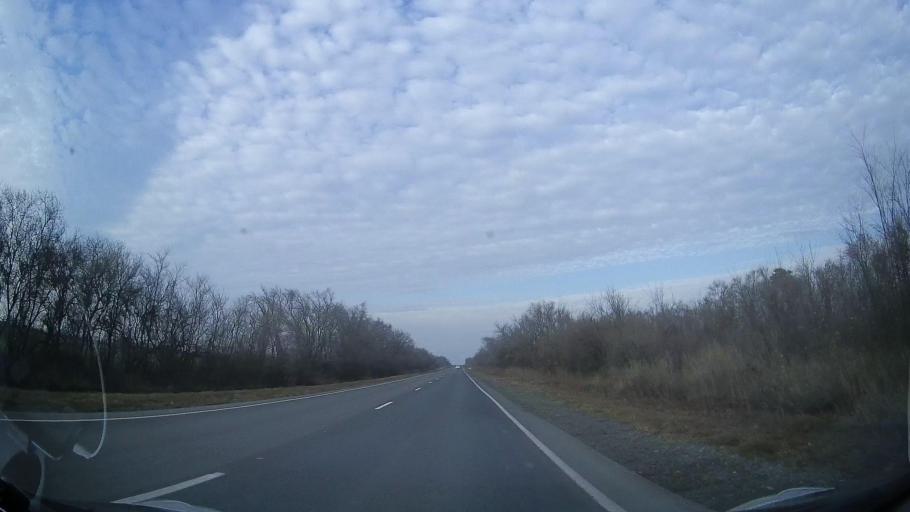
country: RU
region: Rostov
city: Bagayevskaya
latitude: 47.1380
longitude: 40.2767
